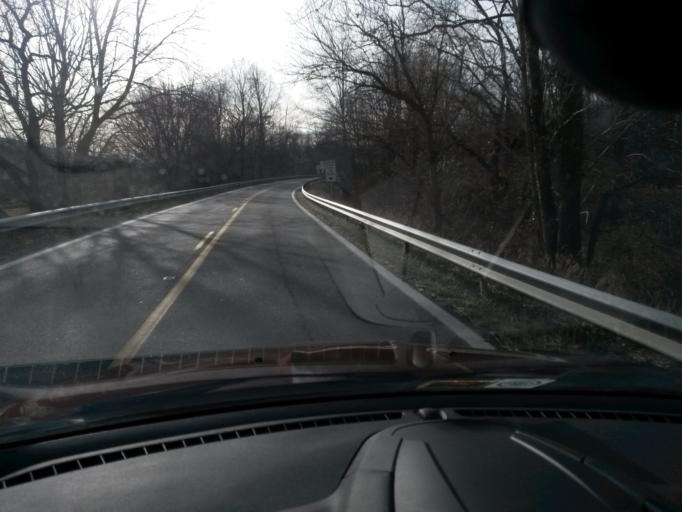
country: US
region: Virginia
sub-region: Rockbridge County
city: East Lexington
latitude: 37.9886
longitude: -79.4927
